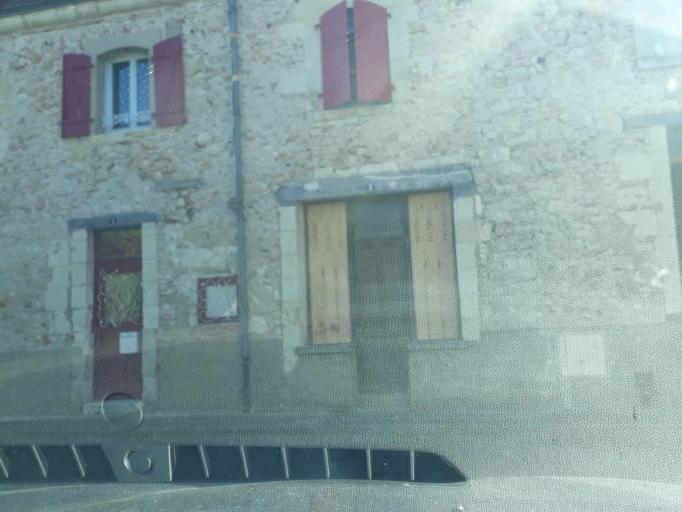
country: FR
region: Centre
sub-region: Departement de l'Indre
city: Chabris
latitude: 47.2559
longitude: 1.6533
